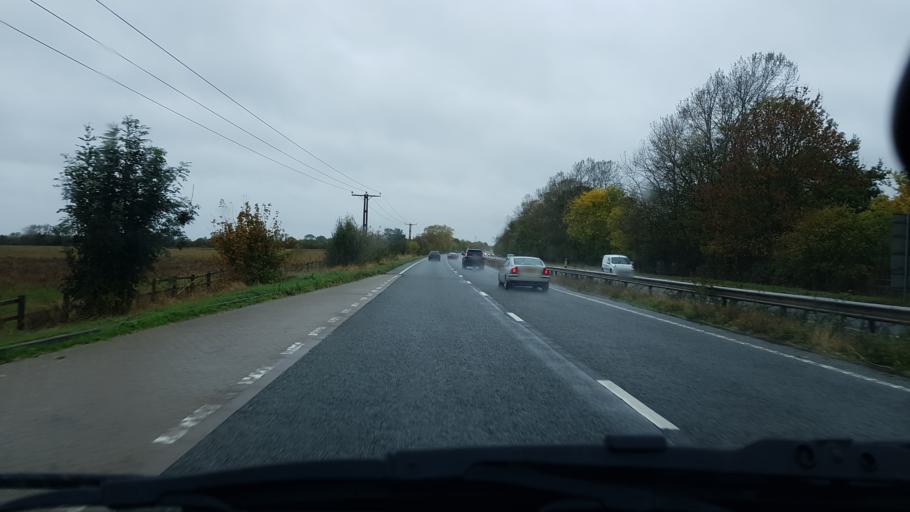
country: GB
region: England
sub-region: Oxfordshire
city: Witney
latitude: 51.7756
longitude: -1.5008
